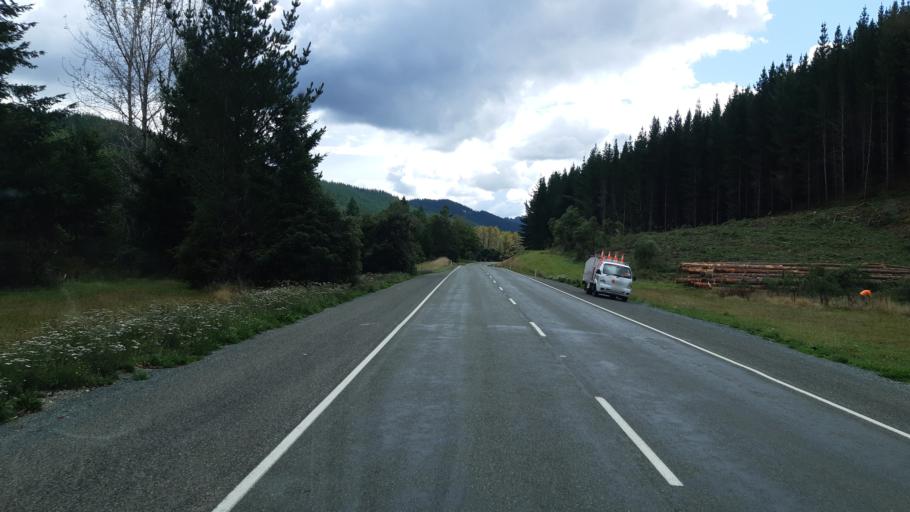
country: NZ
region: Tasman
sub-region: Tasman District
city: Wakefield
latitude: -41.5912
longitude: 172.7641
